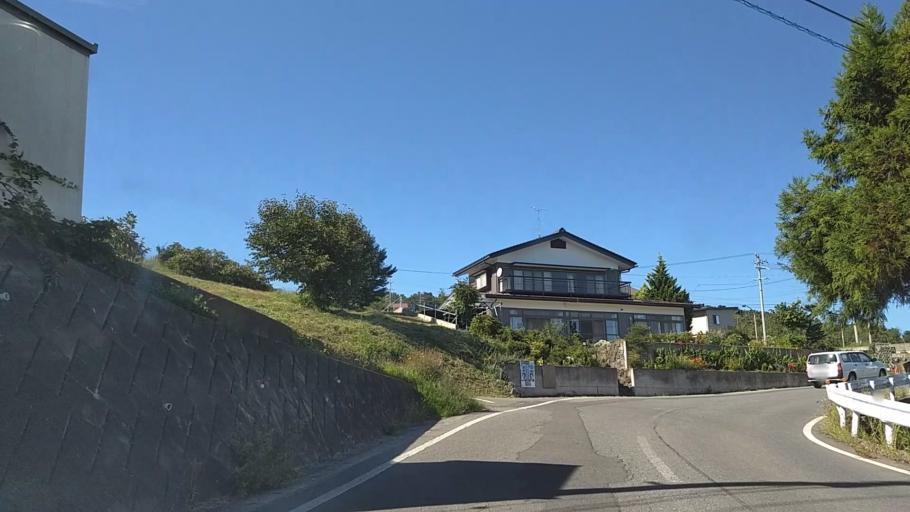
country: JP
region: Nagano
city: Nagano-shi
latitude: 36.5767
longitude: 138.1151
